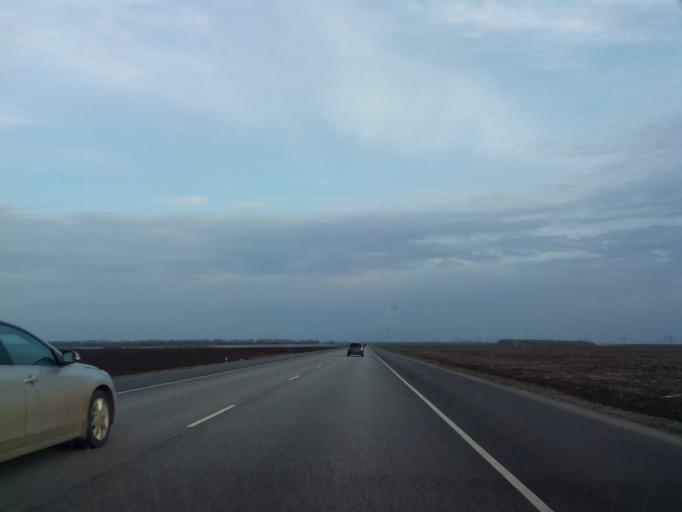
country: RU
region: Rjazan
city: Ryazhsk
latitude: 53.5693
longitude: 40.0476
